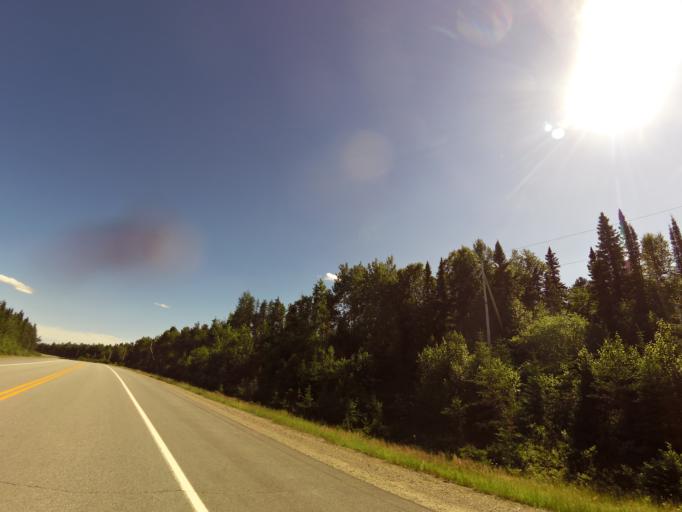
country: CA
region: Quebec
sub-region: Abitibi-Temiscamingue
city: Val-d'Or
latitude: 47.9351
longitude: -77.3609
